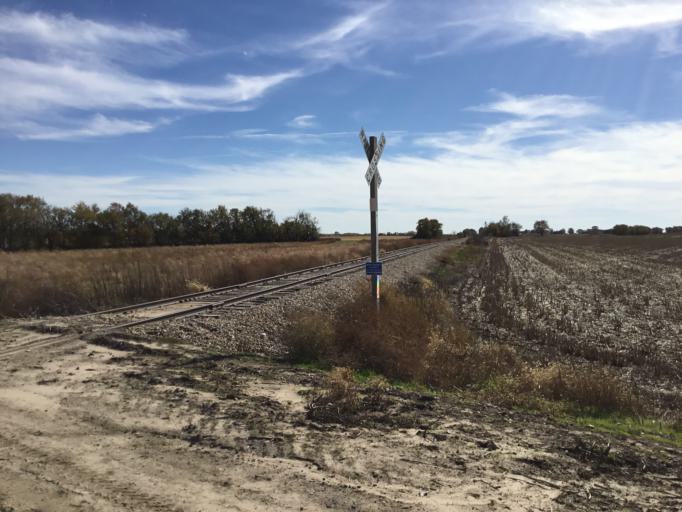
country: US
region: Kansas
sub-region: Lincoln County
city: Lincoln
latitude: 38.9438
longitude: -98.0184
